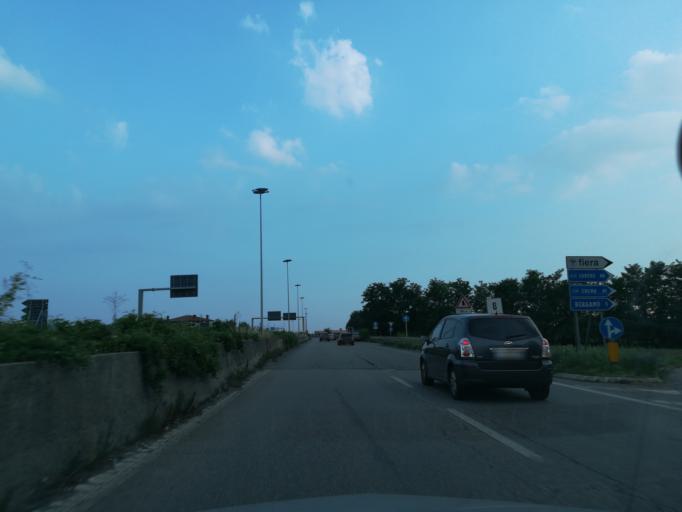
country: IT
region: Lombardy
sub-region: Provincia di Bergamo
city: Treviolo
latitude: 45.6772
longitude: 9.6007
